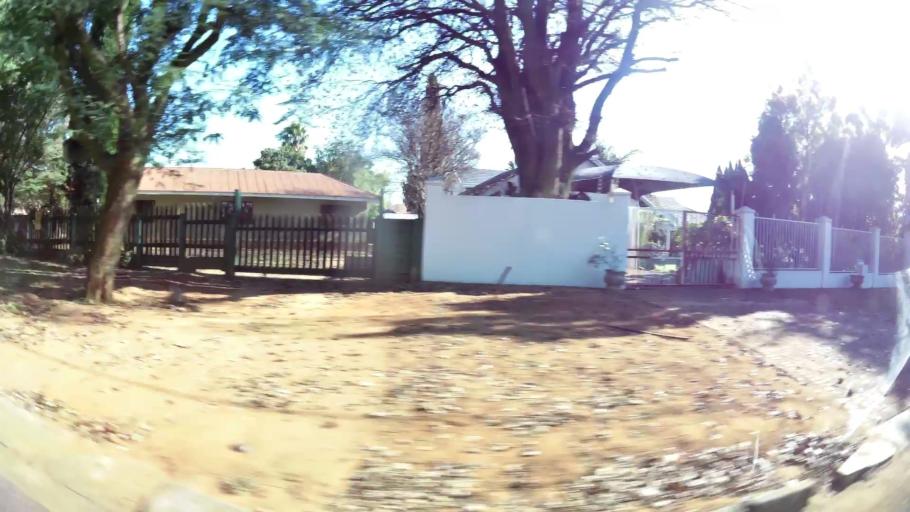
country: ZA
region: Gauteng
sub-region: Ekurhuleni Metropolitan Municipality
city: Benoni
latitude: -26.1528
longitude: 28.3216
